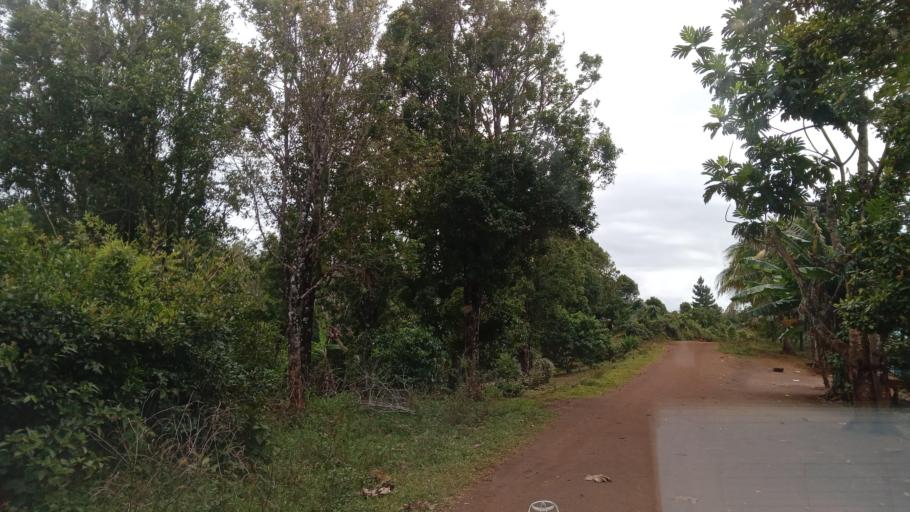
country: MG
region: Atsimo-Atsinanana
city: Vohipaho
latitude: -23.8797
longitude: 47.5331
